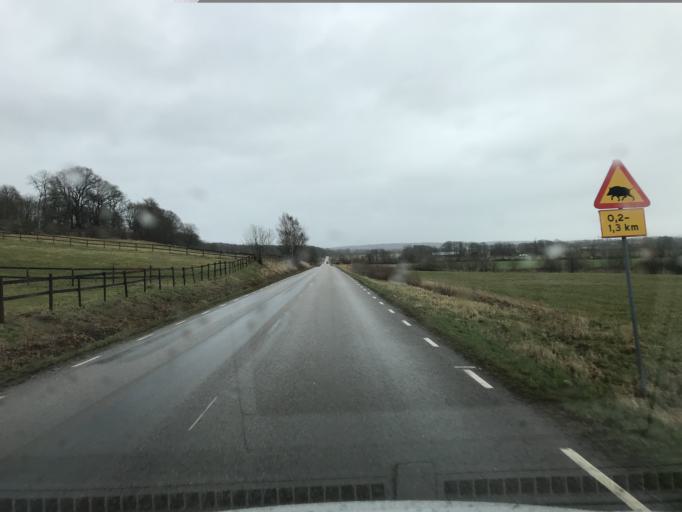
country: SE
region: Skane
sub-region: Bastads Kommun
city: Forslov
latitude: 56.3456
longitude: 12.8632
